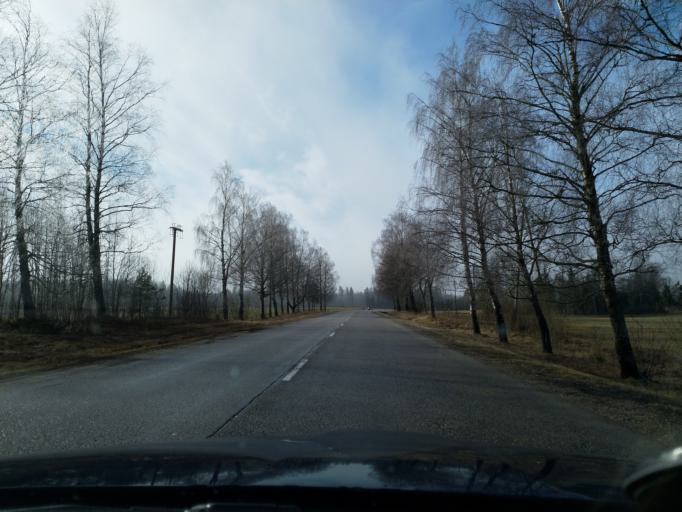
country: LV
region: Kuldigas Rajons
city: Kuldiga
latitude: 56.8963
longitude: 21.8882
